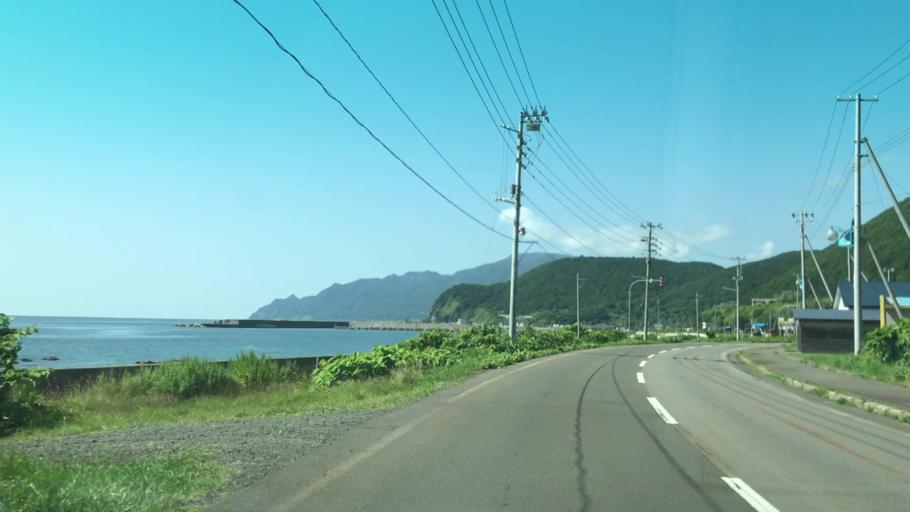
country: JP
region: Hokkaido
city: Iwanai
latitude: 43.0916
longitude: 140.4636
